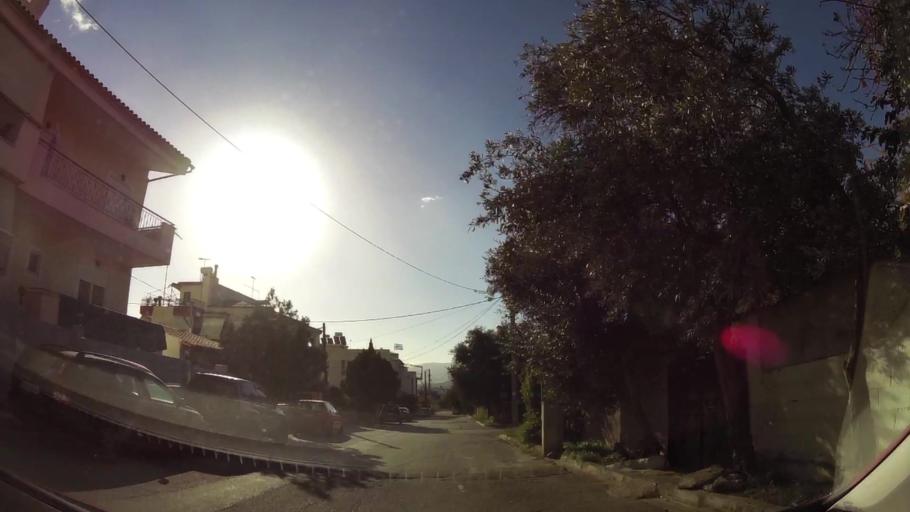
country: GR
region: Attica
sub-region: Nomarchia Anatolikis Attikis
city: Acharnes
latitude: 38.0716
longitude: 23.7429
